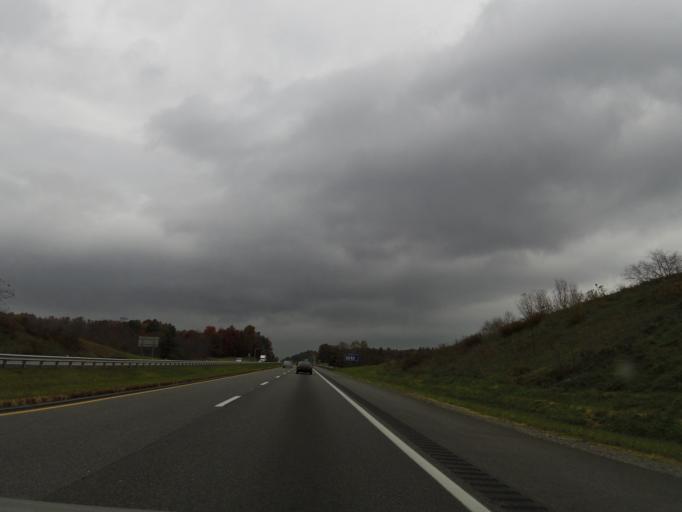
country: US
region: Virginia
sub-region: Bland County
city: Bland
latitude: 37.0776
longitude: -81.1264
